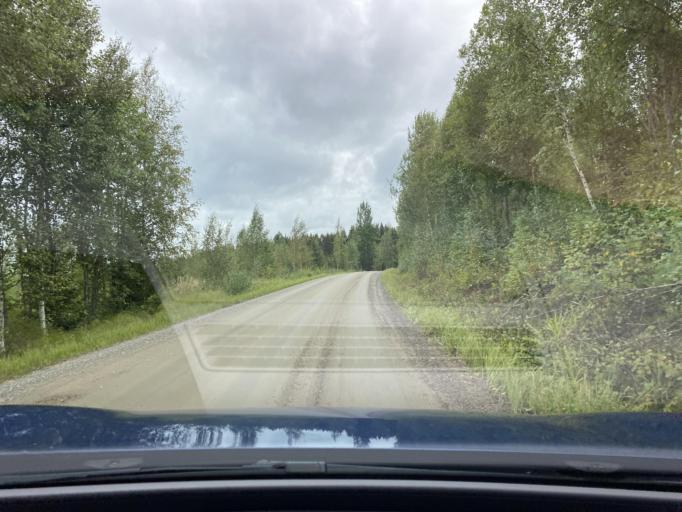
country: FI
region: Pirkanmaa
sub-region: Lounais-Pirkanmaa
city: Punkalaidun
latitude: 61.2202
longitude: 23.1641
